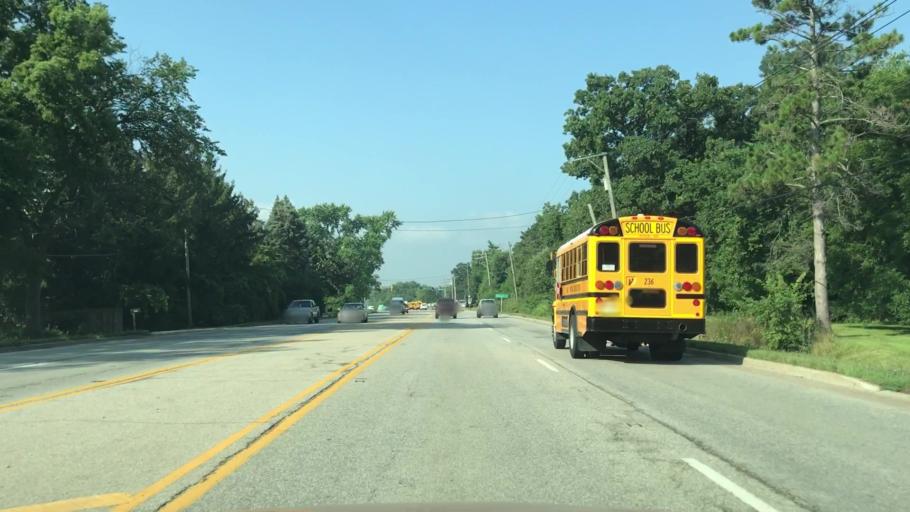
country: US
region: Illinois
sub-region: Will County
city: Romeoville
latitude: 41.6602
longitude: -88.0749
